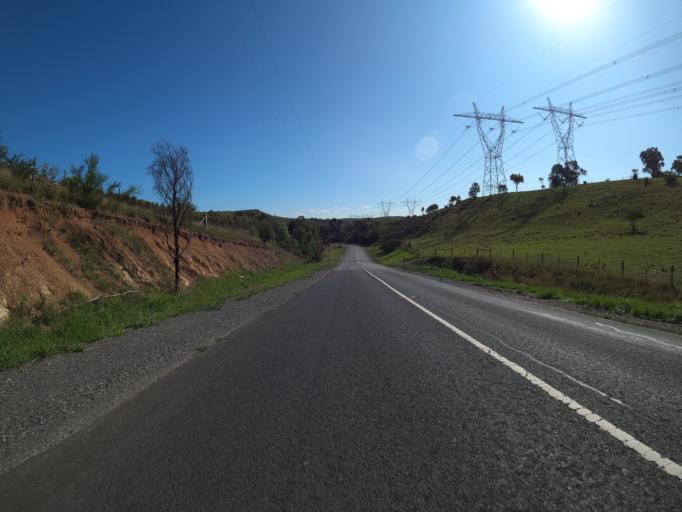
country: AU
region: Victoria
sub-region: Hume
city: Greenvale
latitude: -37.5535
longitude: 144.8535
